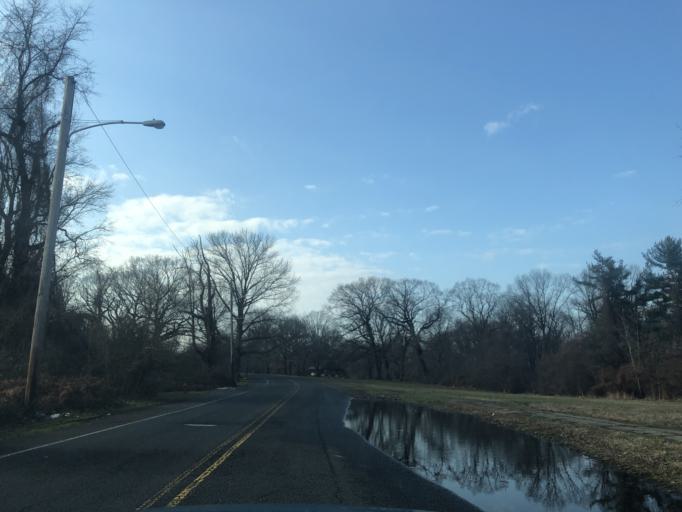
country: US
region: Pennsylvania
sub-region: Montgomery County
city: Bala-Cynwyd
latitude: 39.9885
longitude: -75.2208
